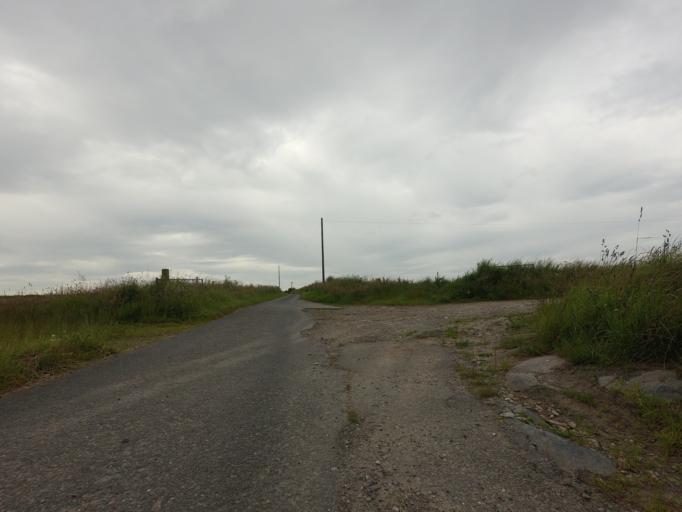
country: GB
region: Scotland
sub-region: Aberdeenshire
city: Whitehills
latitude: 57.6749
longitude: -2.5975
